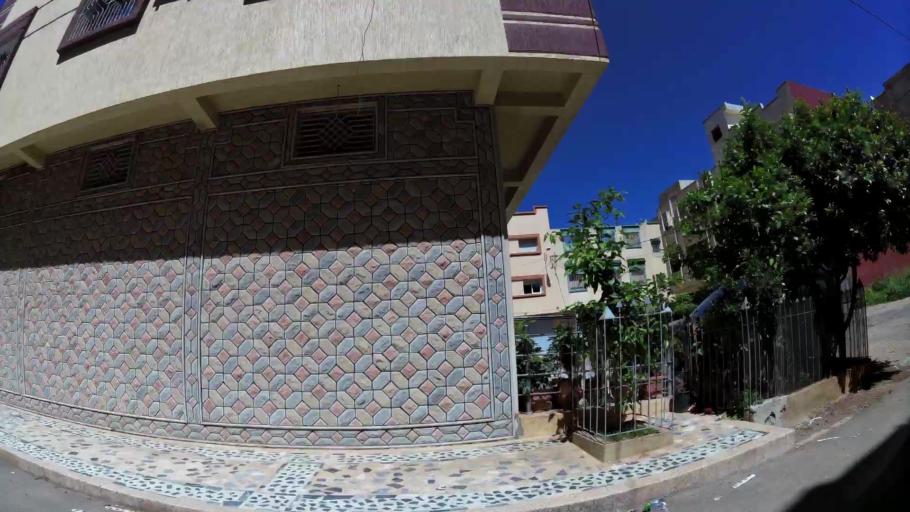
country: MA
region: Meknes-Tafilalet
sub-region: Meknes
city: Meknes
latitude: 33.8985
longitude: -5.5815
